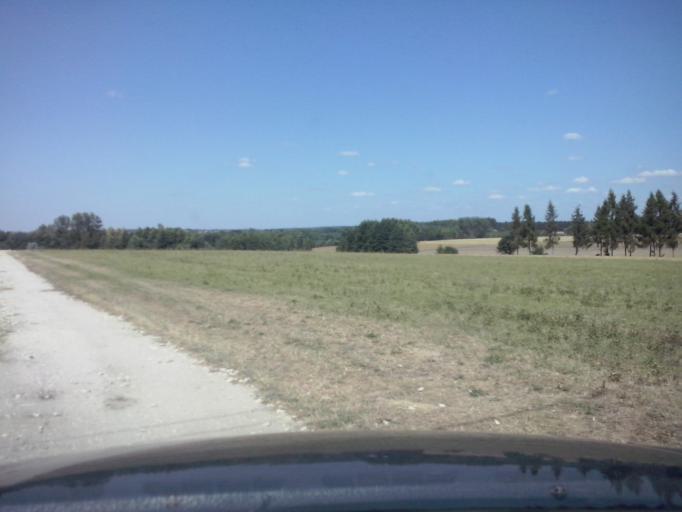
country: PL
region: Swietokrzyskie
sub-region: Powiat buski
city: Gnojno
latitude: 50.5986
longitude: 20.9009
